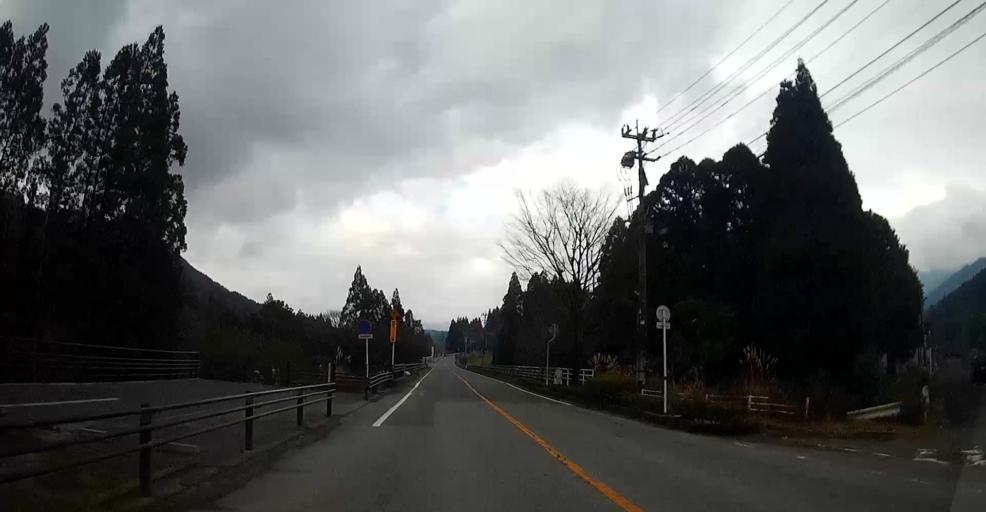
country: JP
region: Kumamoto
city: Matsubase
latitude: 32.6222
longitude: 130.8289
